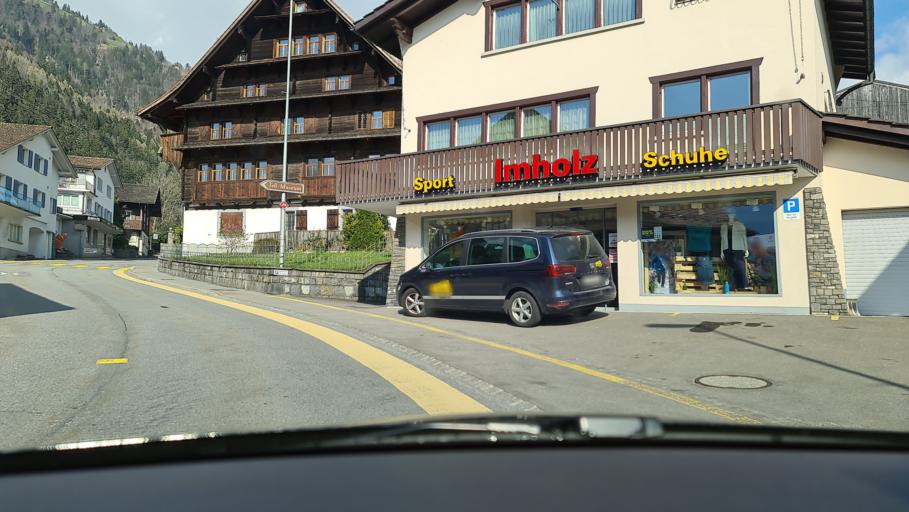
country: CH
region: Uri
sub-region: Uri
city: Burglen
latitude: 46.8753
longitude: 8.6631
